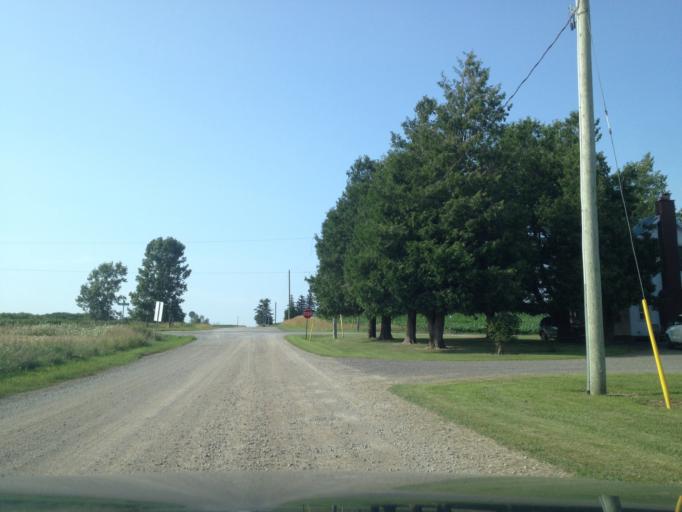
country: CA
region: Ontario
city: Ingersoll
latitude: 42.9604
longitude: -80.7749
